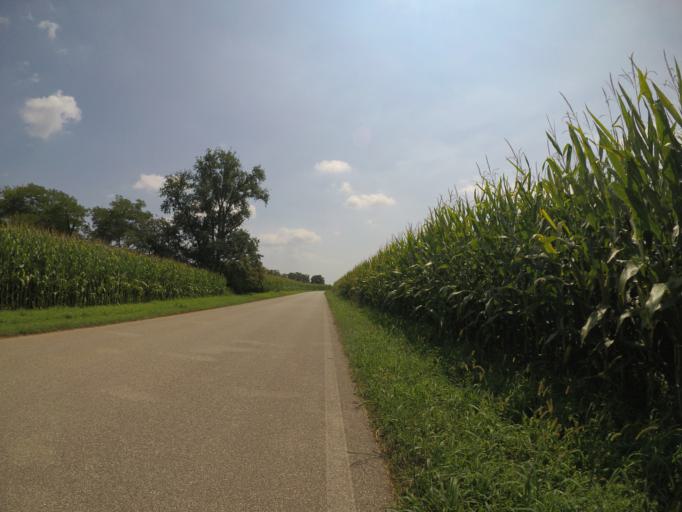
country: IT
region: Friuli Venezia Giulia
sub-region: Provincia di Udine
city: Bertiolo
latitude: 45.9665
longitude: 13.0735
